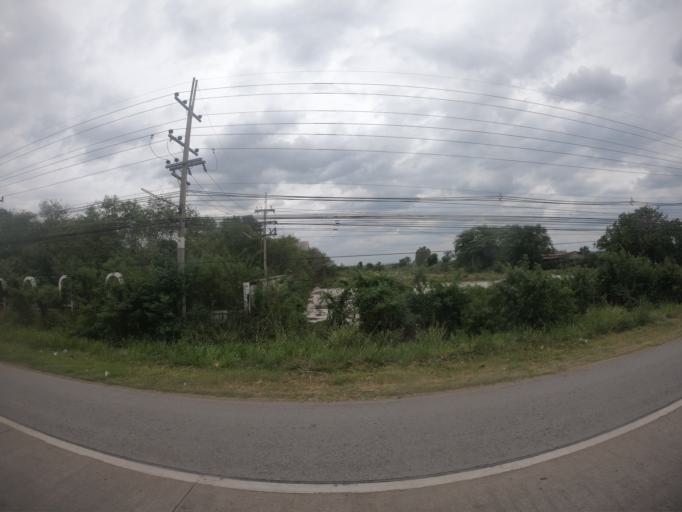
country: TH
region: Nakhon Ratchasima
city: Chok Chai
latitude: 14.7785
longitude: 102.1629
